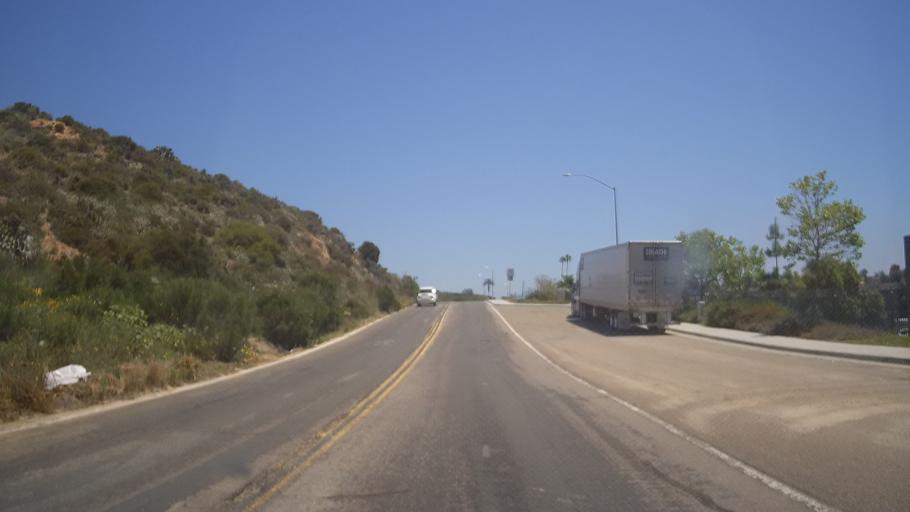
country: US
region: California
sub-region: San Diego County
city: National City
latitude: 32.7104
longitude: -117.0794
